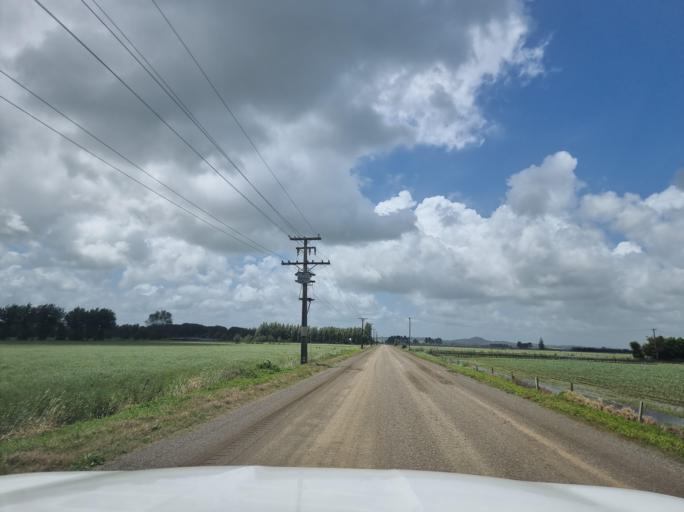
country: NZ
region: Northland
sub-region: Kaipara District
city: Dargaville
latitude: -36.0865
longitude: 174.0009
